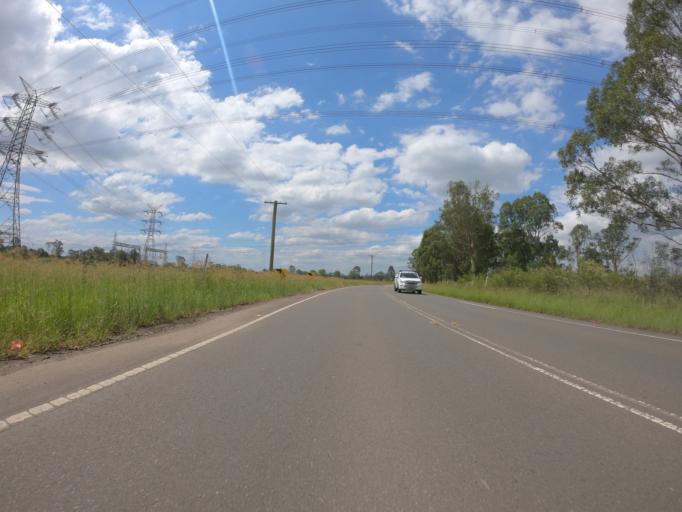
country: AU
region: New South Wales
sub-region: Penrith Municipality
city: Kingswood Park
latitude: -33.8121
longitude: 150.7605
